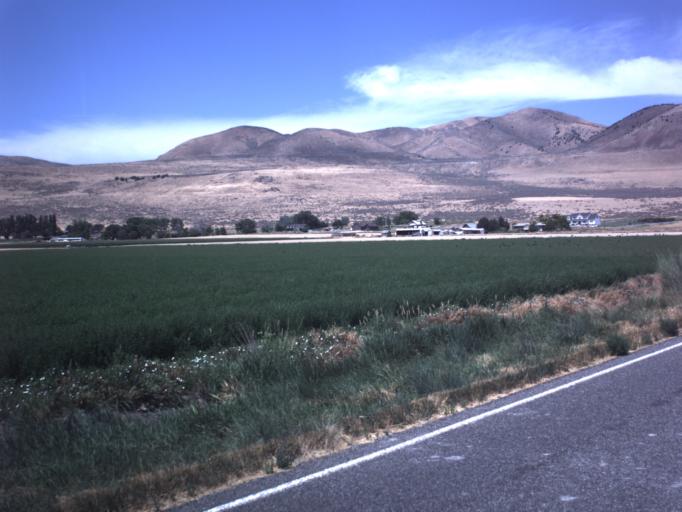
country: US
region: Utah
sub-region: Box Elder County
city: Tremonton
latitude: 41.6462
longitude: -112.3142
